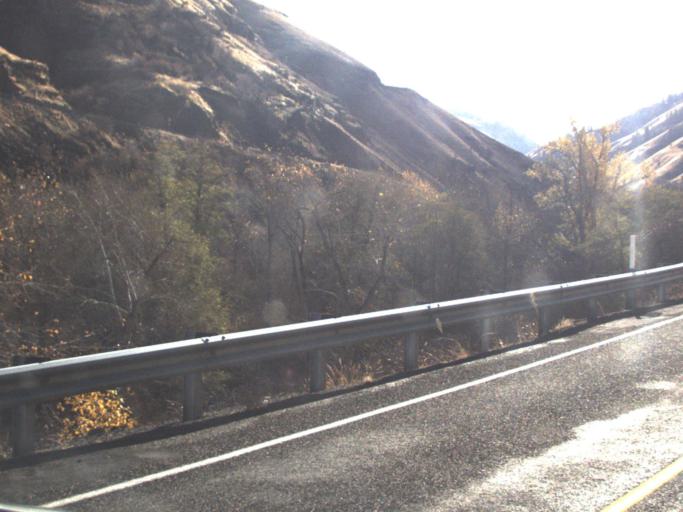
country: US
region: Washington
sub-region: Asotin County
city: Asotin
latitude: 46.0020
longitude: -117.2808
